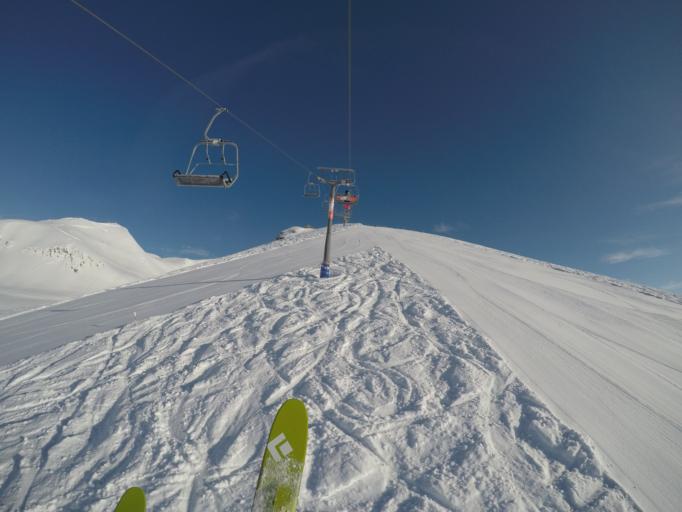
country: GE
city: Gudauri
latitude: 42.4947
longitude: 44.5054
